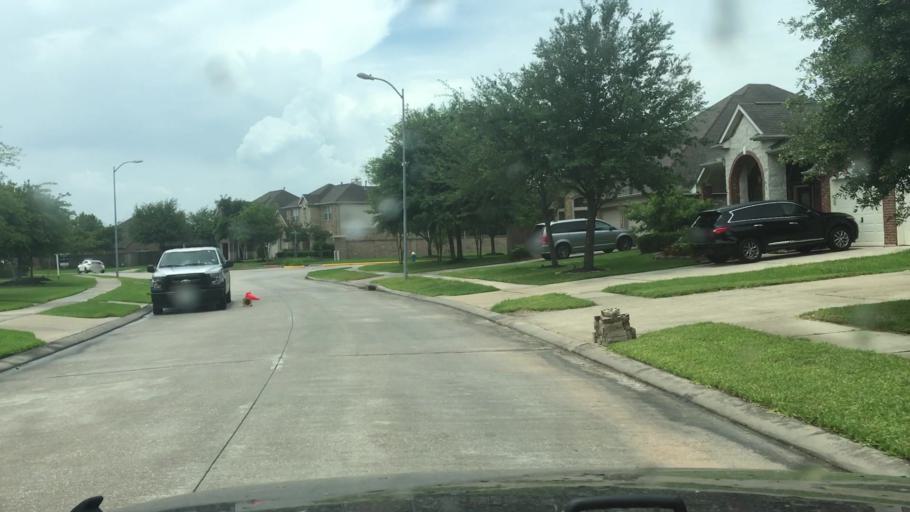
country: US
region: Texas
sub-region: Harris County
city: Humble
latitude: 29.9310
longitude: -95.2496
